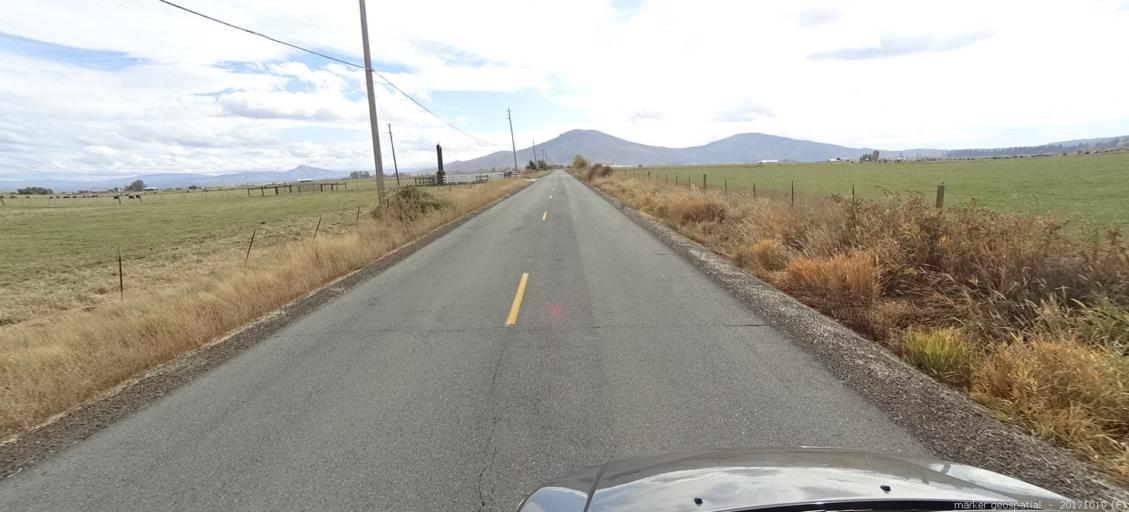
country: US
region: California
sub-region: Shasta County
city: Burney
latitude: 41.0860
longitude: -121.4933
